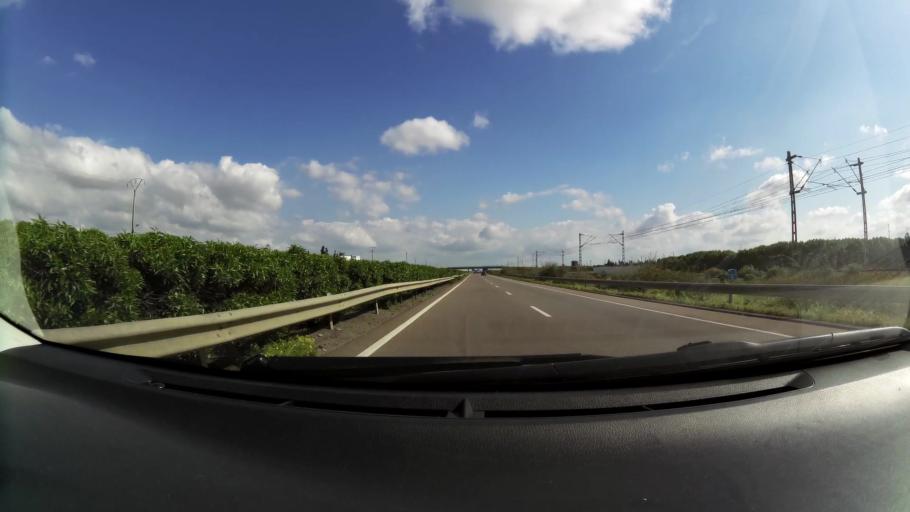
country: MA
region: Chaouia-Ouardigha
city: Nouaseur
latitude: 33.3378
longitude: -7.6113
